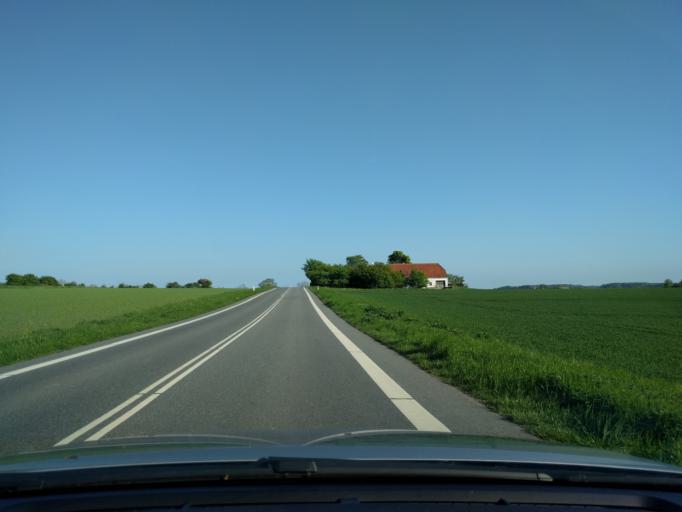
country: DK
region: South Denmark
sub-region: Kerteminde Kommune
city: Kerteminde
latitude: 55.4715
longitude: 10.6713
